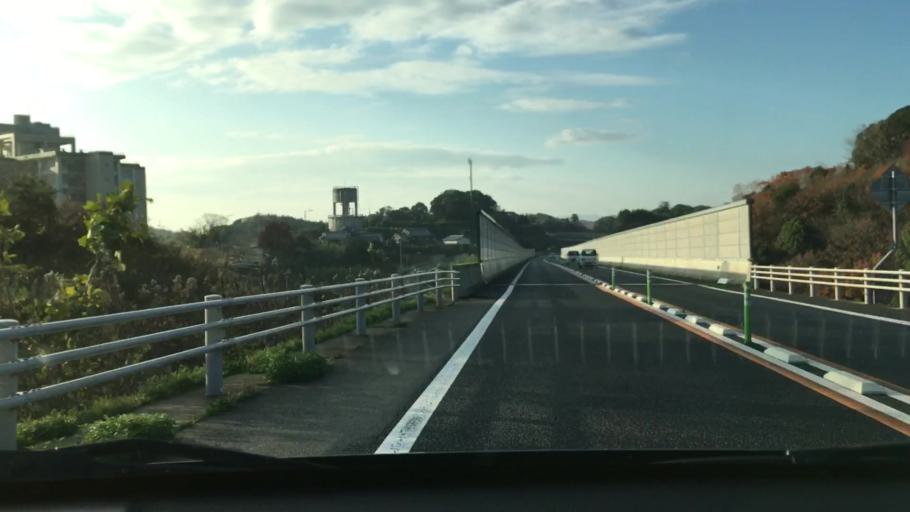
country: JP
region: Nagasaki
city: Sasebo
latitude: 33.0851
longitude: 129.7772
